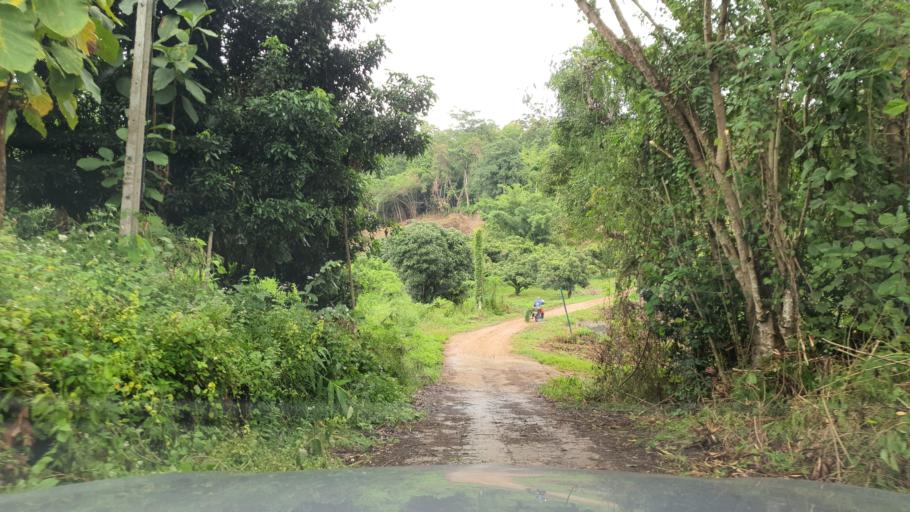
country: TH
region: Chiang Mai
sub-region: Amphoe Chiang Dao
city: Chiang Dao
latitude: 19.3397
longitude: 98.9276
